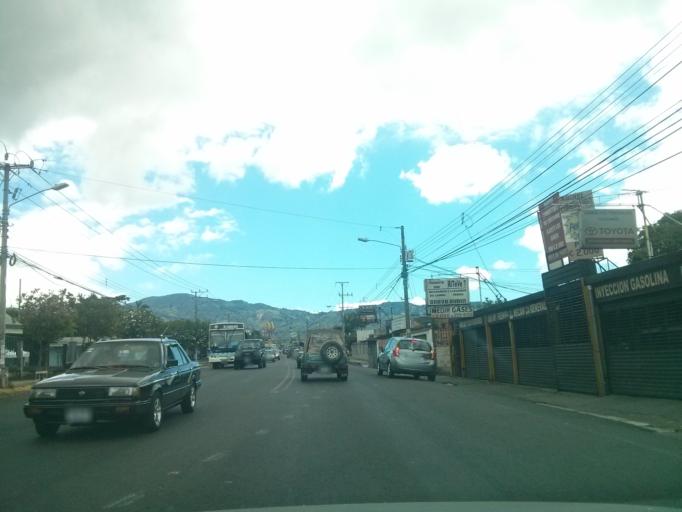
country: CR
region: San Jose
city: San Rafael Arriba
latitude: 9.8946
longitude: -84.0644
